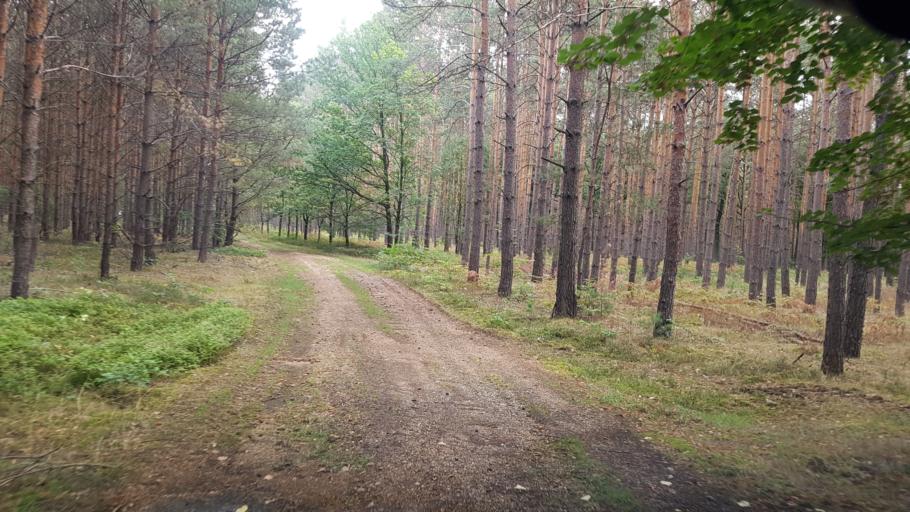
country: DE
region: Brandenburg
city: Crinitz
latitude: 51.7104
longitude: 13.7693
